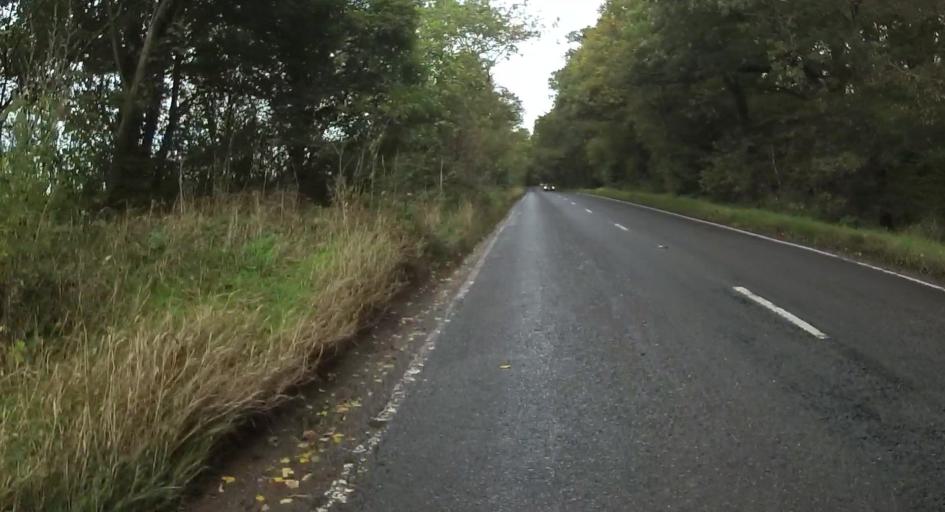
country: GB
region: England
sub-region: Hampshire
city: Odiham
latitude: 51.2686
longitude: -0.9274
